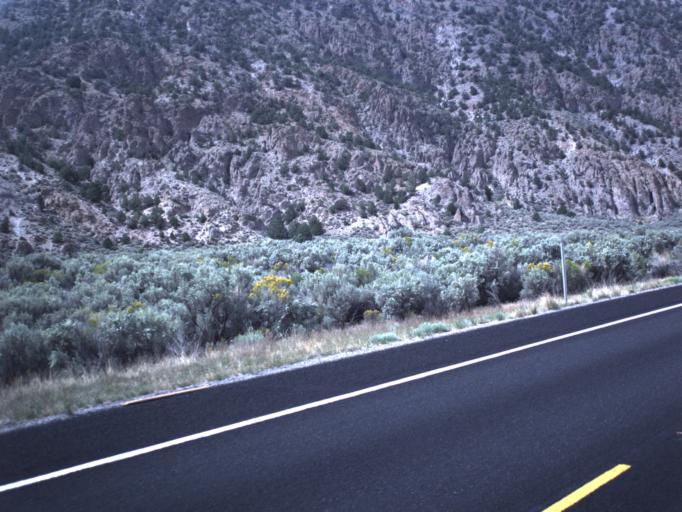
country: US
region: Utah
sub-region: Piute County
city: Junction
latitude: 38.0632
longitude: -112.3482
